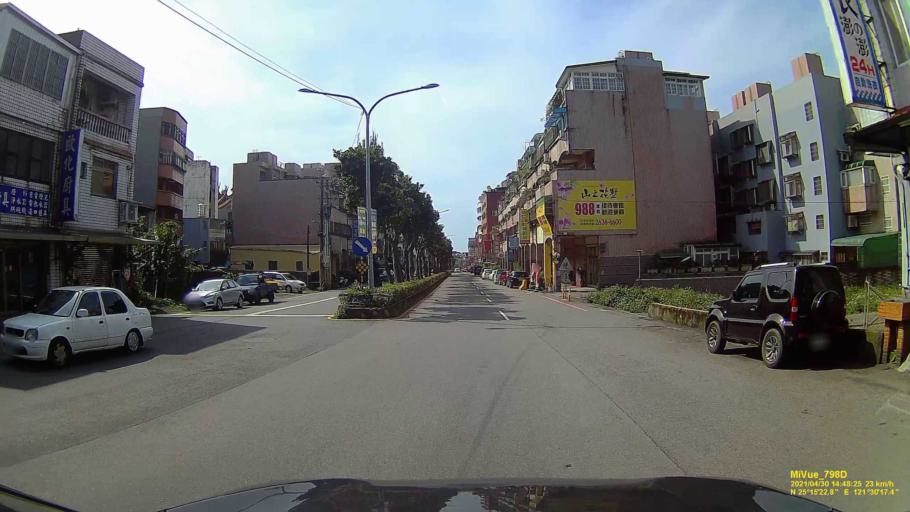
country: TW
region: Taipei
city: Taipei
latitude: 25.2564
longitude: 121.5048
